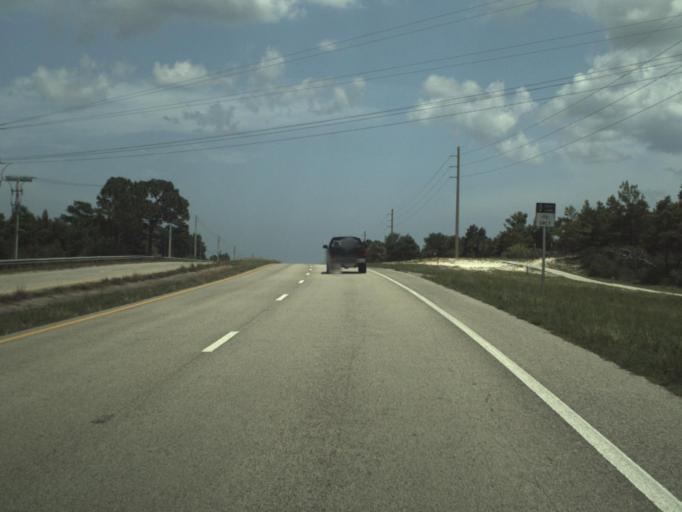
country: US
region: Florida
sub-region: Martin County
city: Hobe Sound
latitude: 27.0535
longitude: -80.1328
